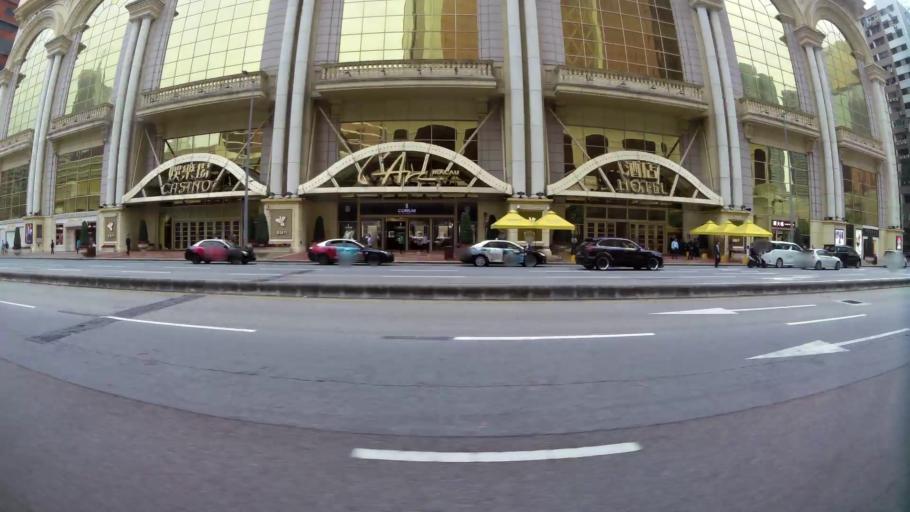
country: MO
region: Macau
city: Macau
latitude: 22.1883
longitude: 113.5478
